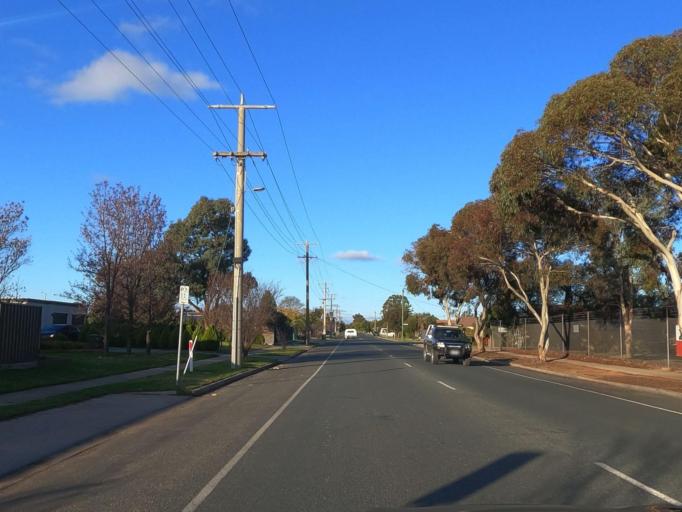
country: AU
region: Victoria
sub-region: Swan Hill
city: Swan Hill
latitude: -35.3465
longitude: 143.5455
